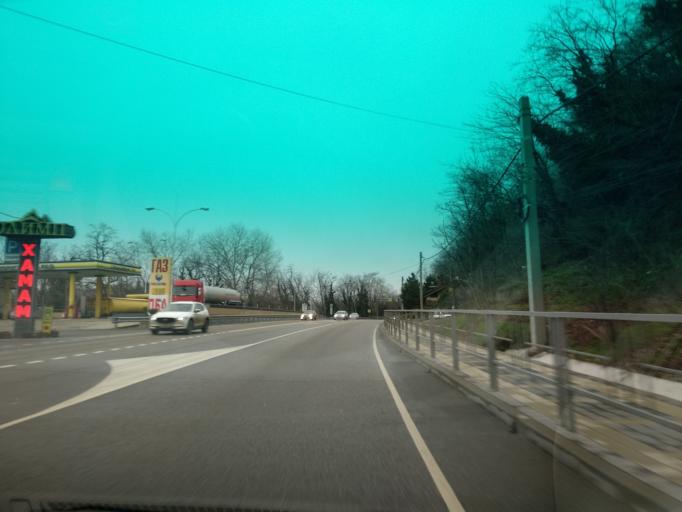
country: RU
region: Krasnodarskiy
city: Tuapse
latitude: 44.1060
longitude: 39.0750
